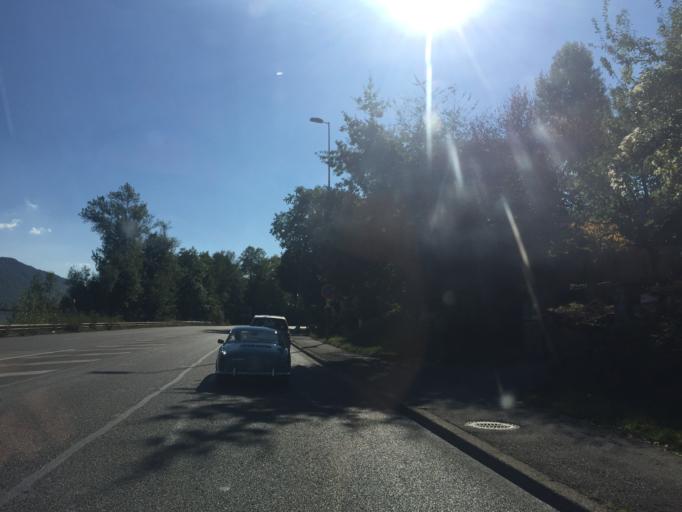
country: FR
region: Rhone-Alpes
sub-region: Departement de la Haute-Savoie
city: Annecy
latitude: 45.8911
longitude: 6.1098
